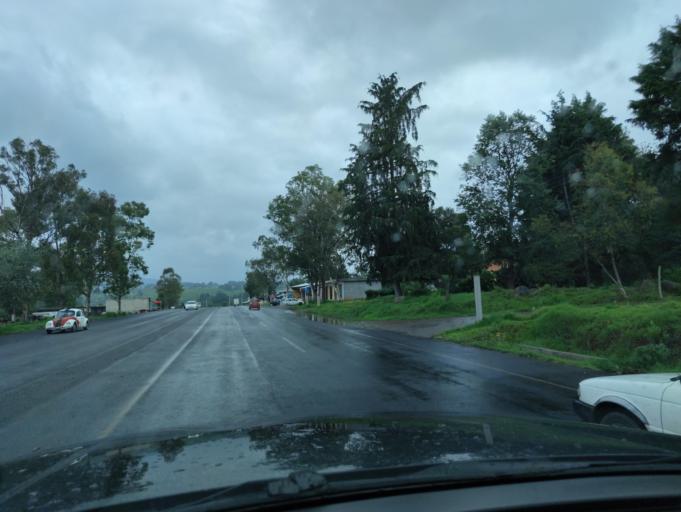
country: MX
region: Mexico
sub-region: Jilotepec
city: Doxhicho
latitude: 19.9115
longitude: -99.6075
